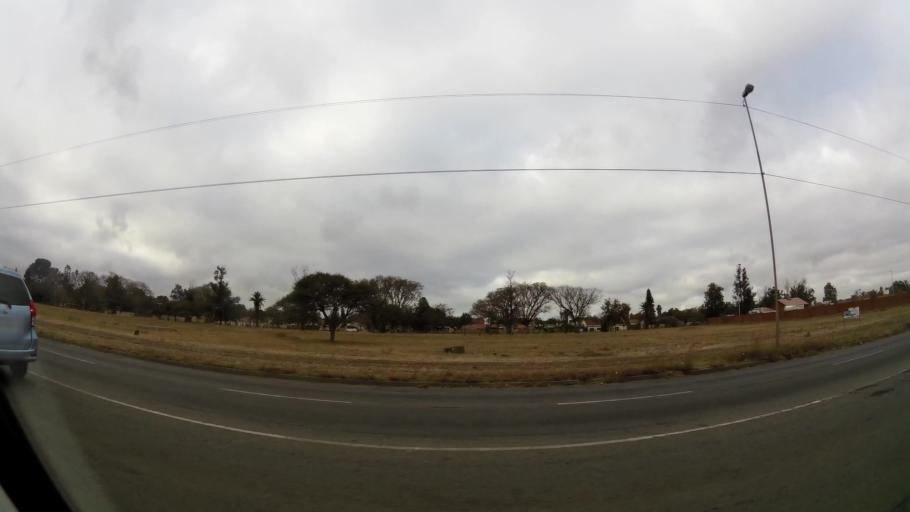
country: ZA
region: Limpopo
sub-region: Capricorn District Municipality
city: Polokwane
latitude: -23.8748
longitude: 29.4469
